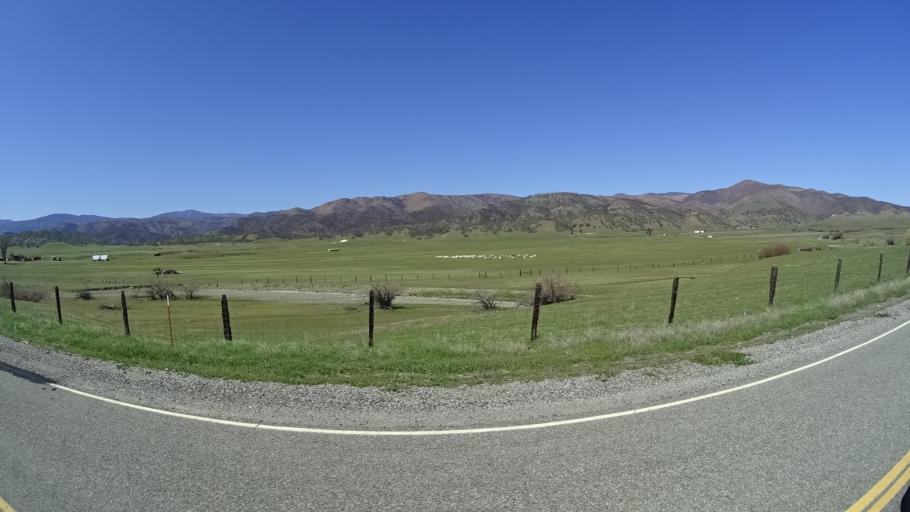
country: US
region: California
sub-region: Tehama County
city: Rancho Tehama Reserve
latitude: 39.6965
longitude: -122.5495
